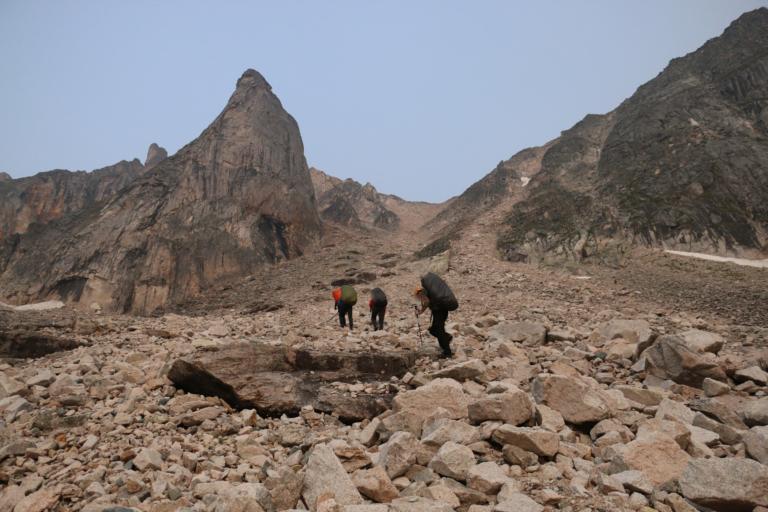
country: RU
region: Respublika Buryatiya
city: Novyy Uoyan
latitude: 56.2136
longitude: 111.0048
